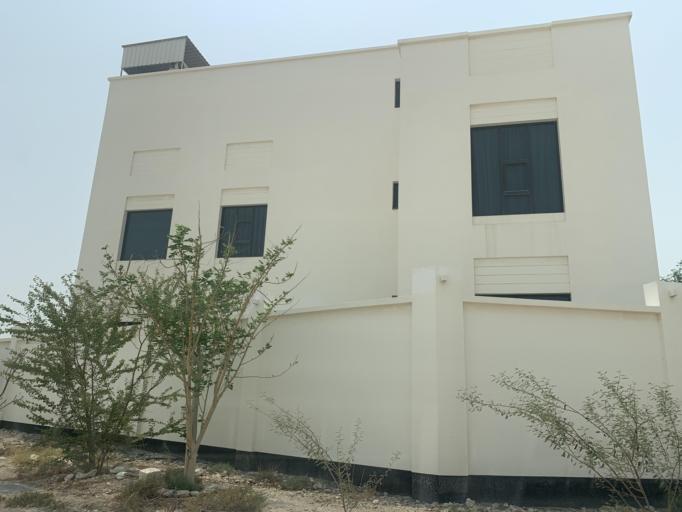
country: BH
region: Central Governorate
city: Madinat Hamad
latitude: 26.1601
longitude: 50.4816
